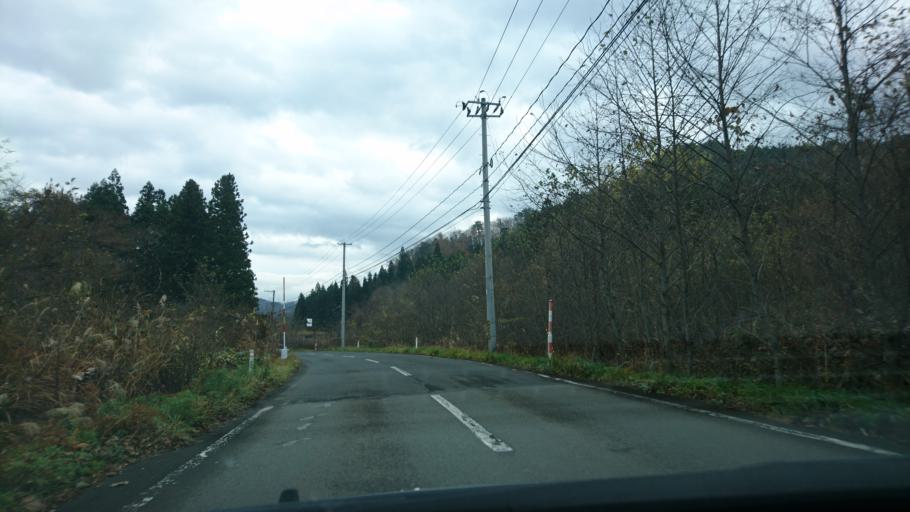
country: JP
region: Iwate
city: Ichinoseki
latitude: 38.9074
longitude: 140.8932
